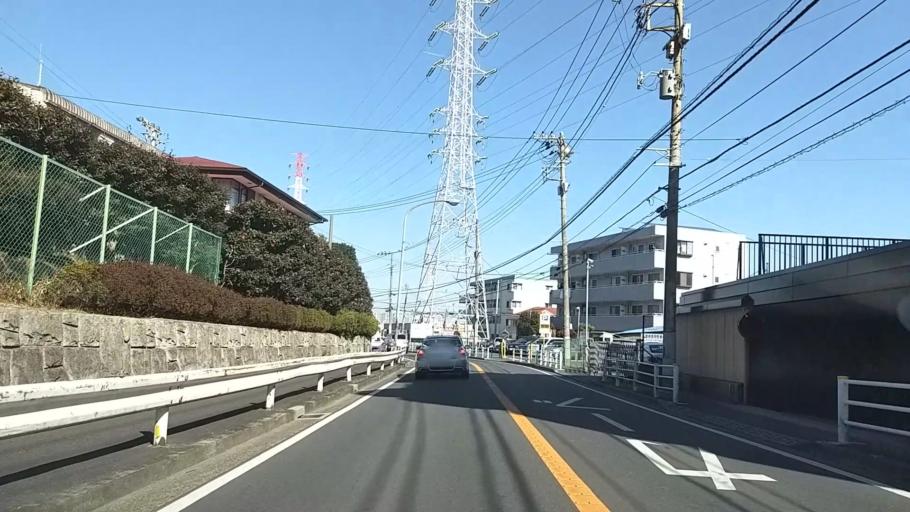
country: JP
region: Kanagawa
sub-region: Kawasaki-shi
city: Kawasaki
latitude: 35.5185
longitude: 139.6498
